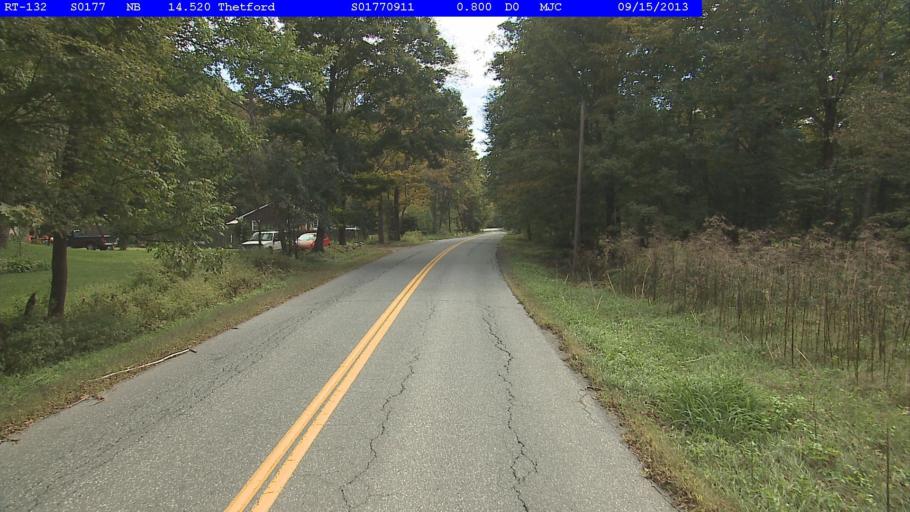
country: US
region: New Hampshire
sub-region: Grafton County
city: Hanover
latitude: 43.8340
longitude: -72.3066
